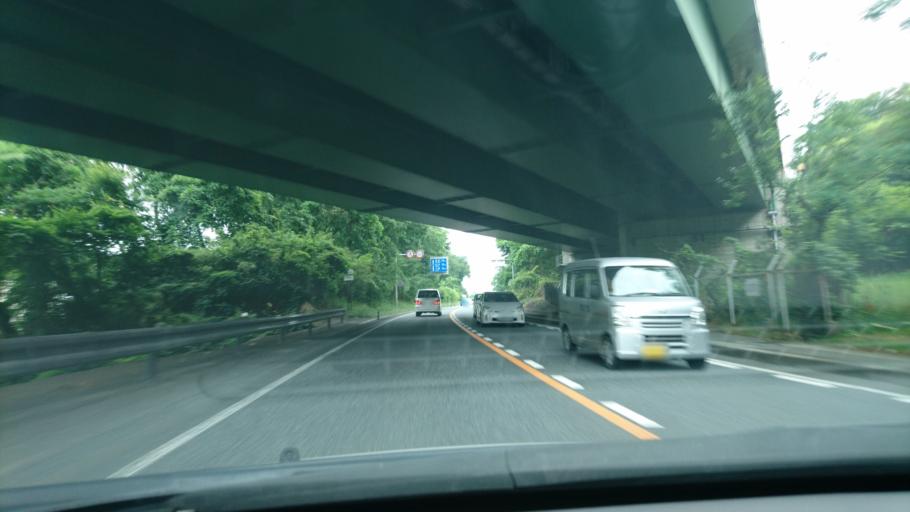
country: JP
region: Miyagi
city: Furukawa
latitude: 38.7188
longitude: 141.0239
